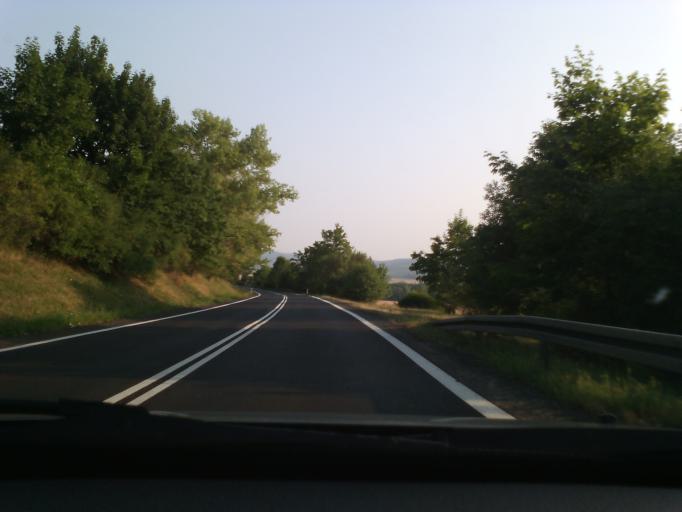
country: PL
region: Lower Silesian Voivodeship
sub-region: Powiat jaworski
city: Bolkow
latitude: 50.9395
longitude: 16.0690
